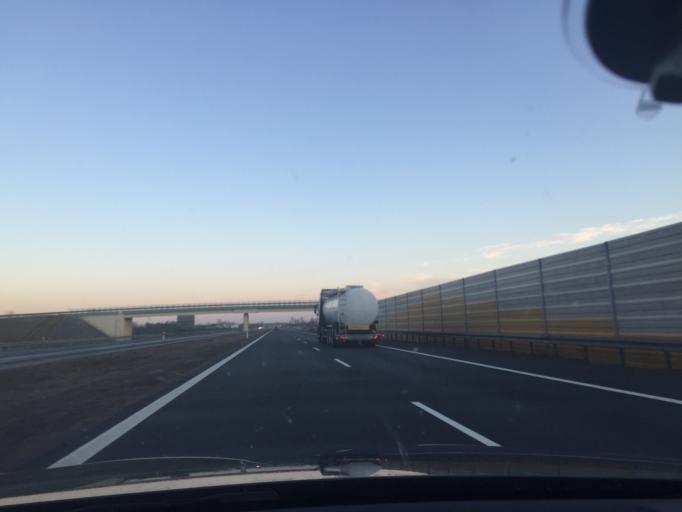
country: PL
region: Greater Poland Voivodeship
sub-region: Powiat kolski
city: Dabie
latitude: 52.0597
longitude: 18.8345
